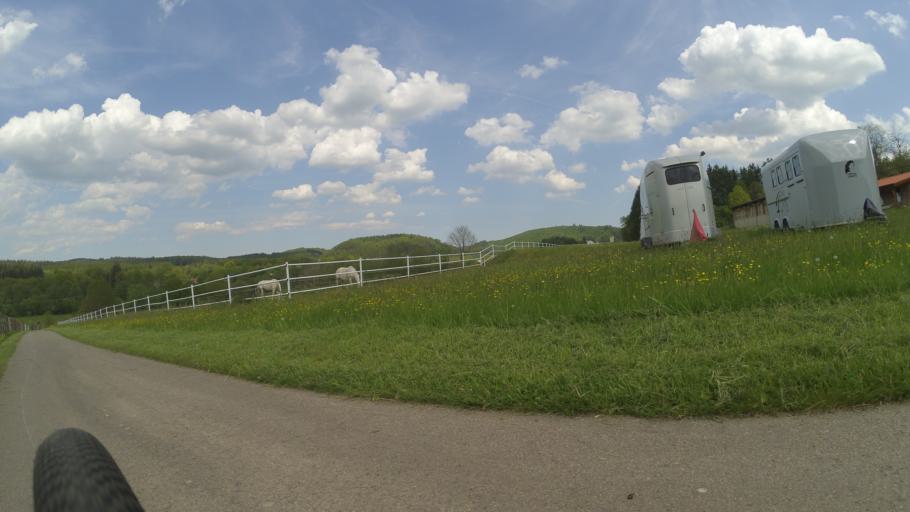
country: DE
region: Rheinland-Pfalz
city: Meckenbach
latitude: 49.5761
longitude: 7.0929
